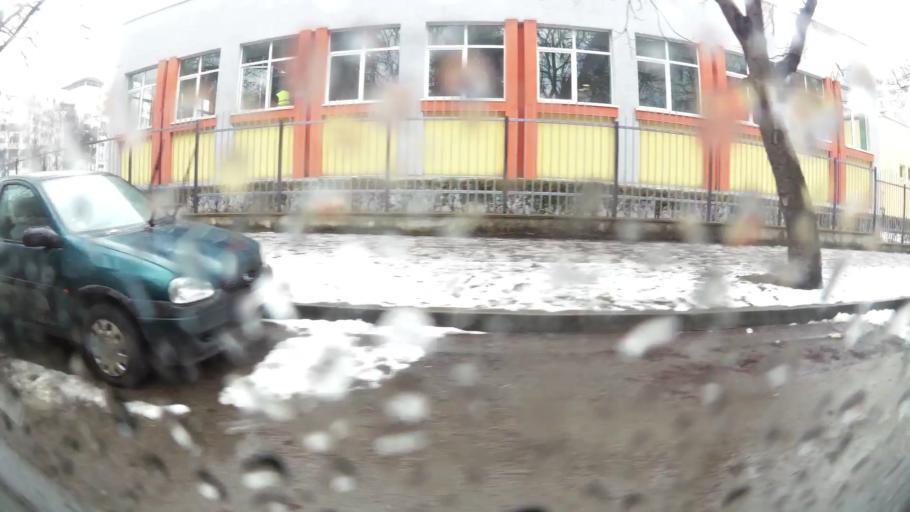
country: BG
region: Sofia-Capital
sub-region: Stolichna Obshtina
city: Sofia
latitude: 42.6753
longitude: 23.3009
